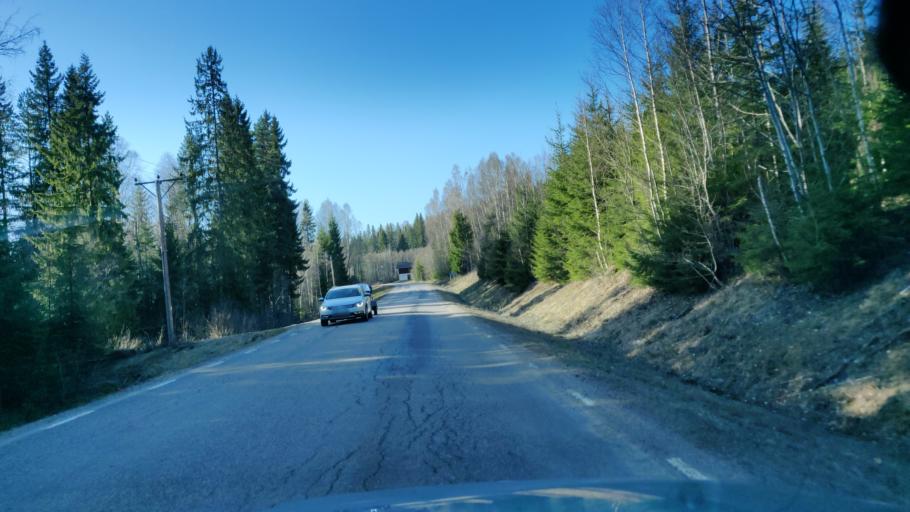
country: SE
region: Vaermland
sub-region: Munkfors Kommun
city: Munkfors
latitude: 59.9817
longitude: 13.4046
